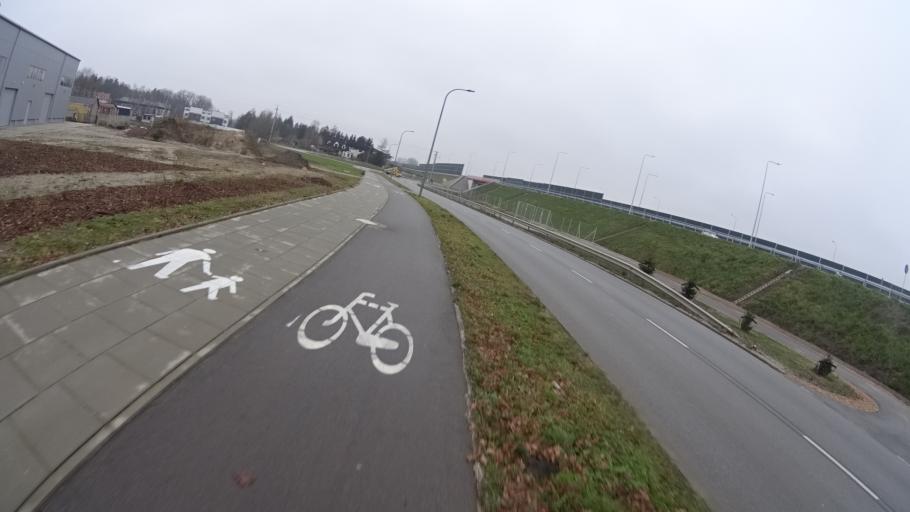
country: PL
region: Masovian Voivodeship
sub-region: Warszawa
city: Wawer
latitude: 52.1630
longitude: 21.1633
